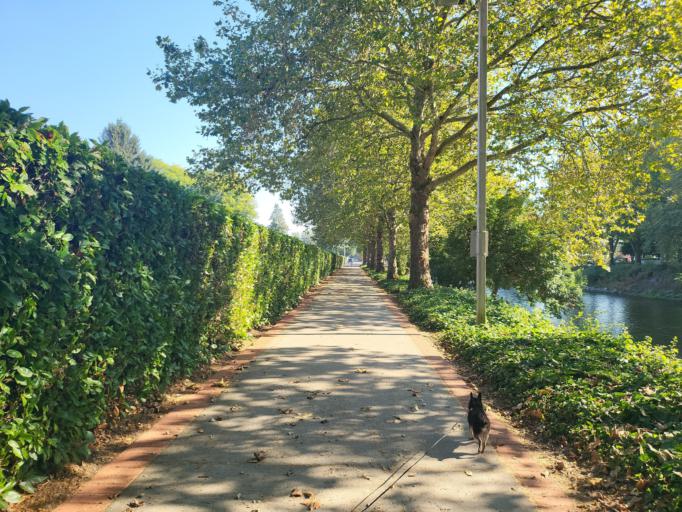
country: US
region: Washington
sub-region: King County
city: Renton
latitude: 47.4851
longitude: -122.2073
